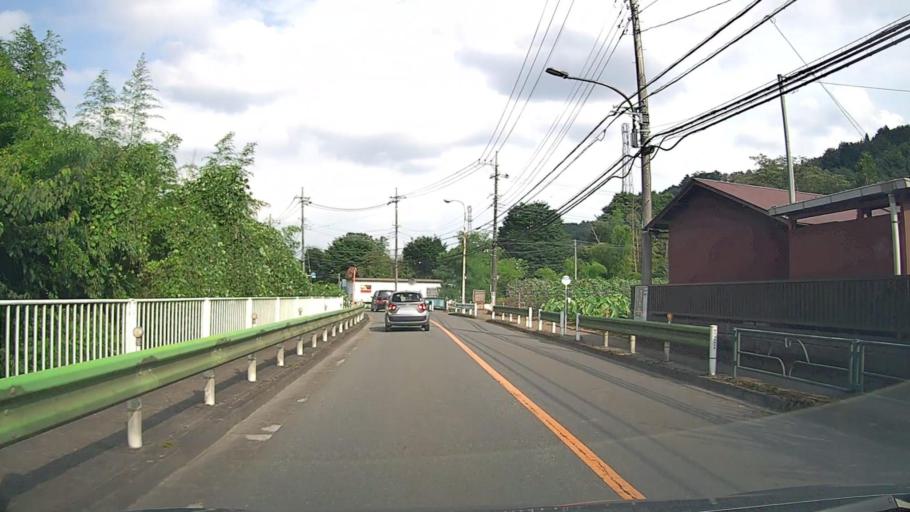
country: JP
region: Tokyo
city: Itsukaichi
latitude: 35.7055
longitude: 139.2460
